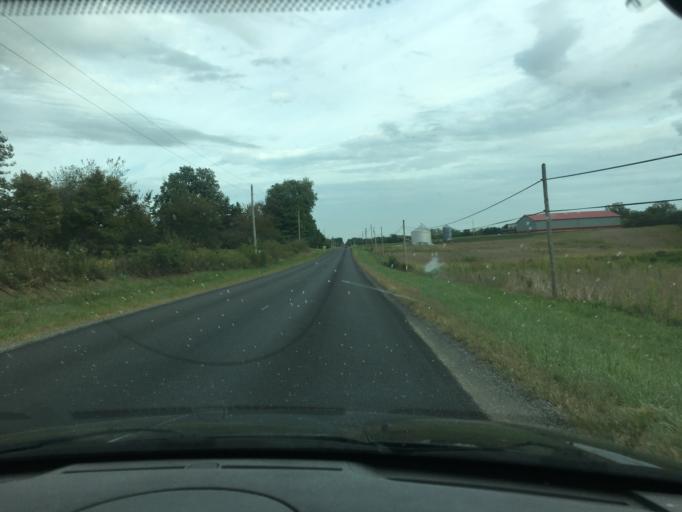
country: US
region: Ohio
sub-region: Logan County
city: Bellefontaine
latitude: 40.3276
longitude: -83.7397
